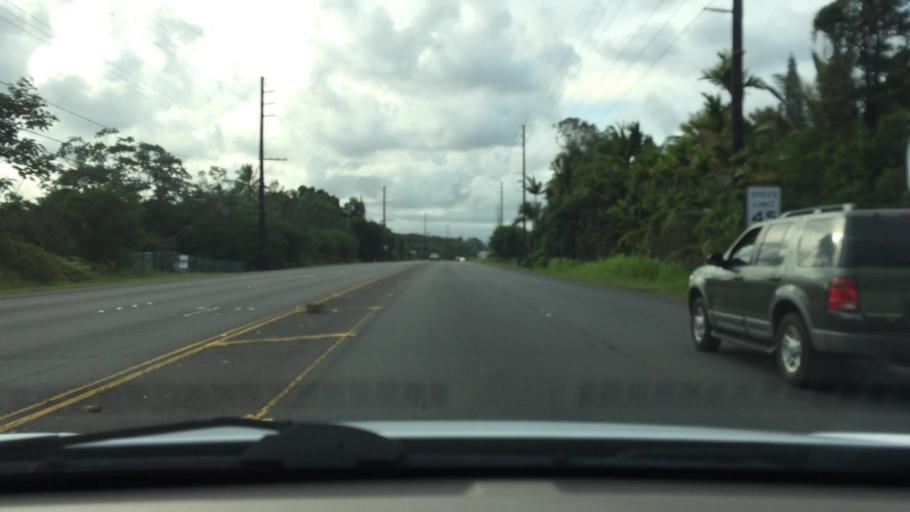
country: US
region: Hawaii
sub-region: Hawaii County
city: Ainaloa
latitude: 19.5471
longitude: -154.9788
